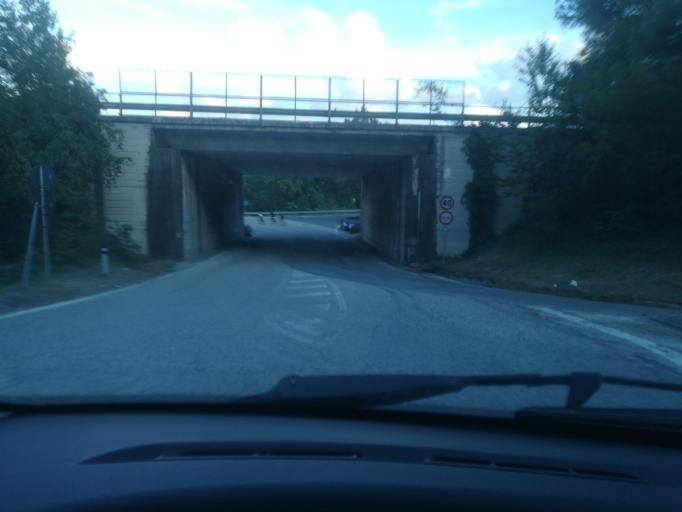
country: IT
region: The Marches
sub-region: Provincia di Macerata
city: Caldarola
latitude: 43.1462
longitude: 13.1985
